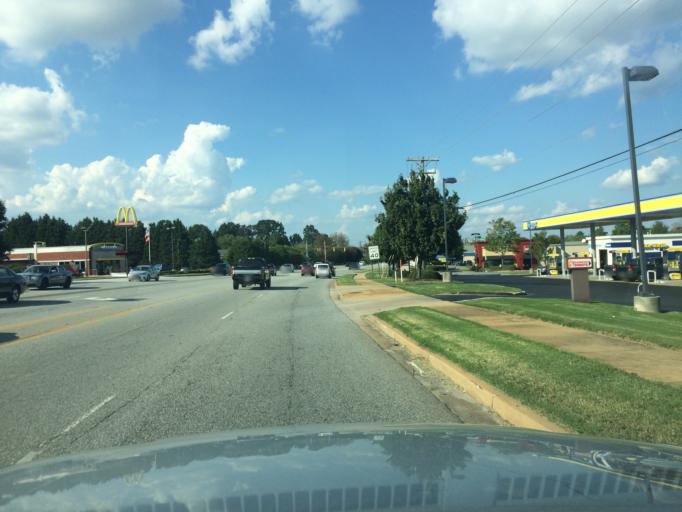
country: US
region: South Carolina
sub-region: Greenville County
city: Simpsonville
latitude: 34.7051
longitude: -82.2578
